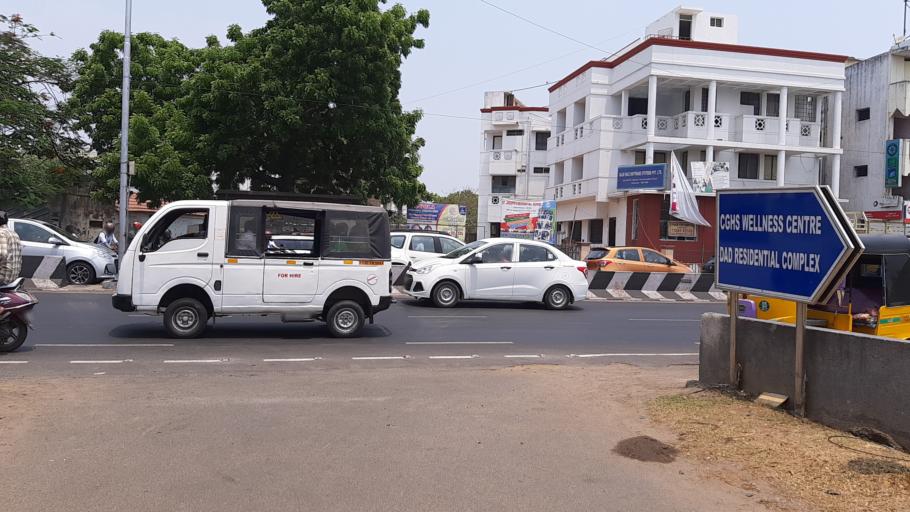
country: IN
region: Tamil Nadu
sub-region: Kancheepuram
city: Saint Thomas Mount
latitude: 13.0137
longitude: 80.1943
